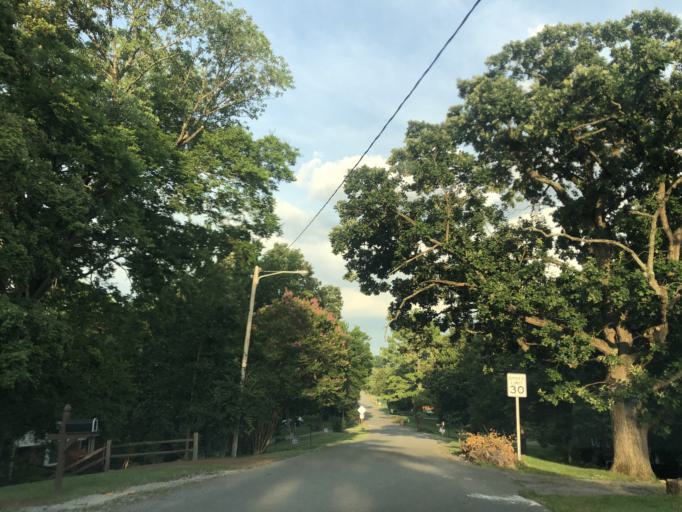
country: US
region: Tennessee
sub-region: Davidson County
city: Nashville
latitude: 36.1683
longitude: -86.7060
